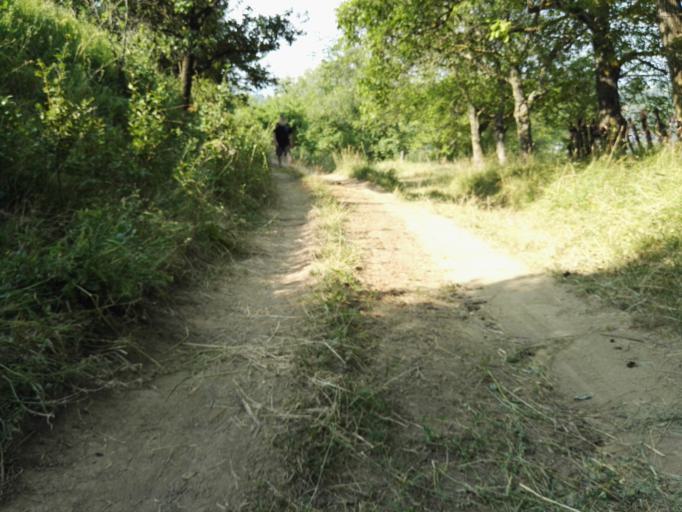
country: RO
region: Suceava
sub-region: Comuna Radaseni
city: Radaseni
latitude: 47.4633
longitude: 26.2616
